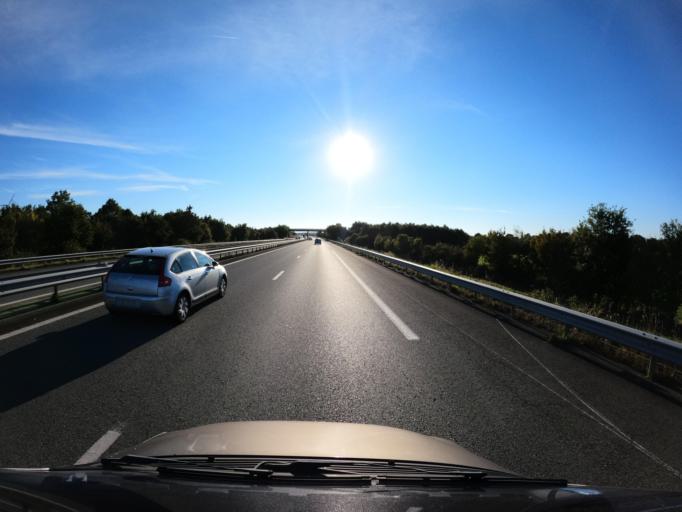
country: FR
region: Pays de la Loire
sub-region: Departement de Maine-et-Loire
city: Trementines
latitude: 47.1714
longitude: -0.7989
